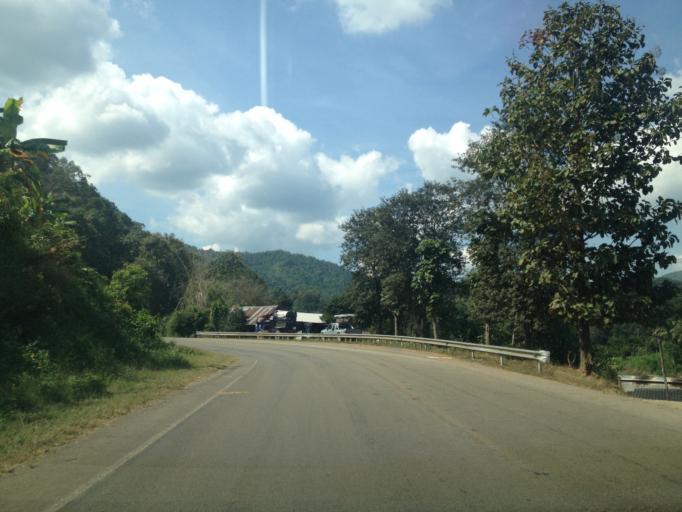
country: TH
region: Chiang Mai
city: Samoeng
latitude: 18.8081
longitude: 98.8245
